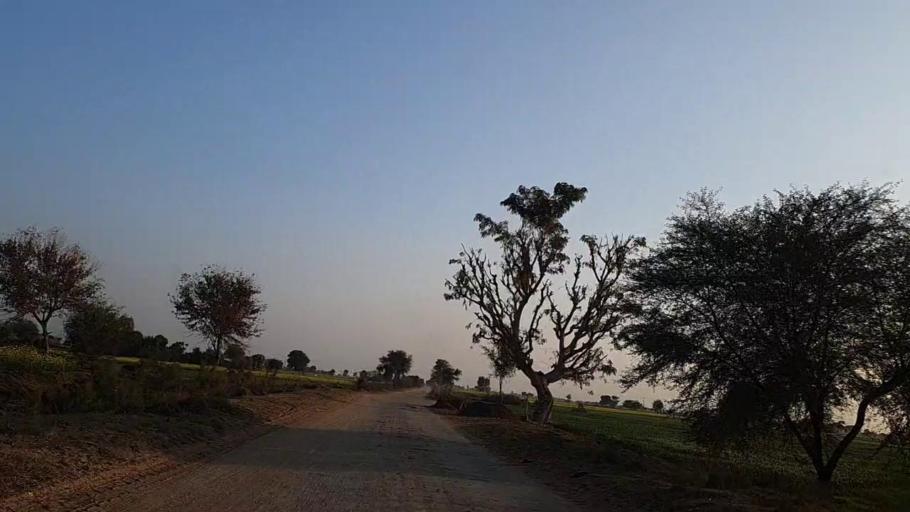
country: PK
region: Sindh
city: Shahdadpur
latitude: 26.0151
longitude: 68.4902
